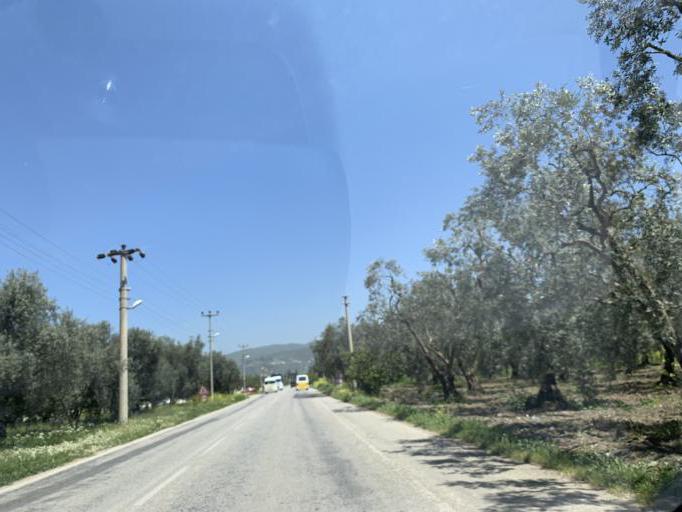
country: TR
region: Bursa
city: Iznik
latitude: 40.4145
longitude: 29.7118
